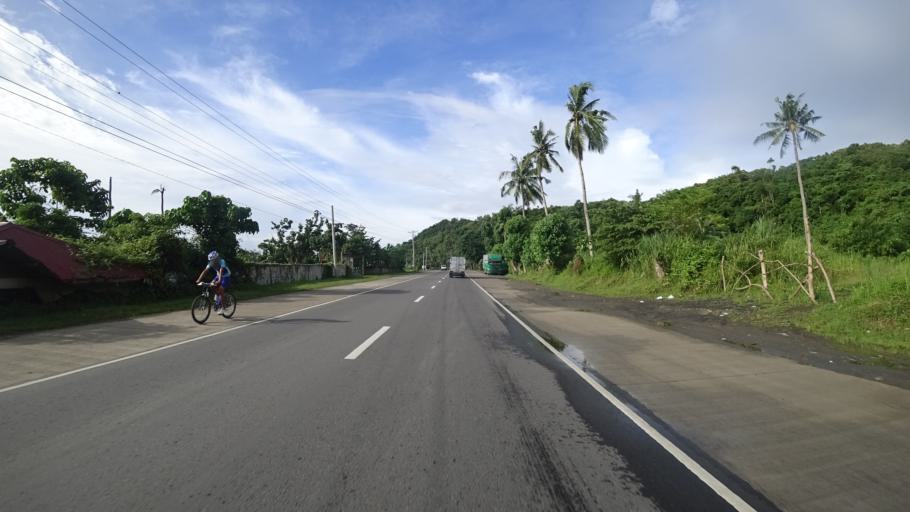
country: PH
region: Eastern Visayas
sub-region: Province of Leyte
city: Tolosa
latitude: 11.0931
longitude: 125.0210
